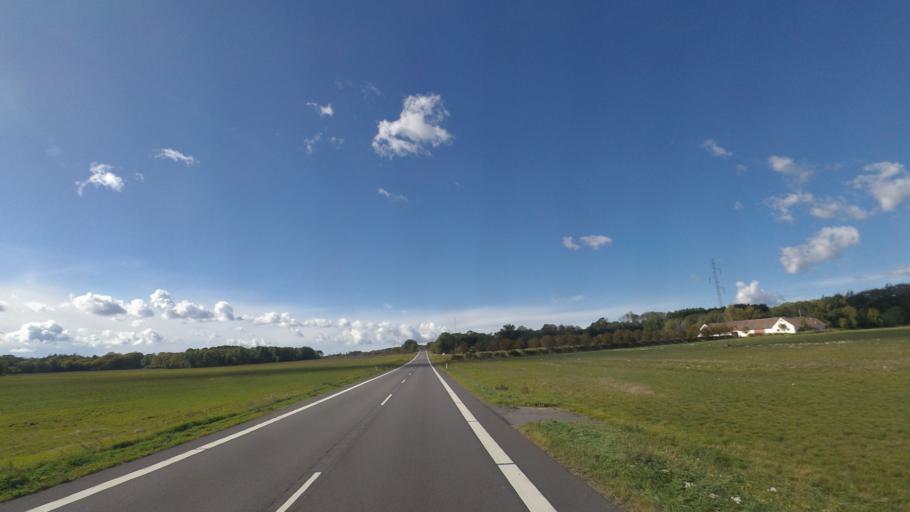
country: DK
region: Capital Region
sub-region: Bornholm Kommune
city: Nexo
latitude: 55.0612
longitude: 15.0427
